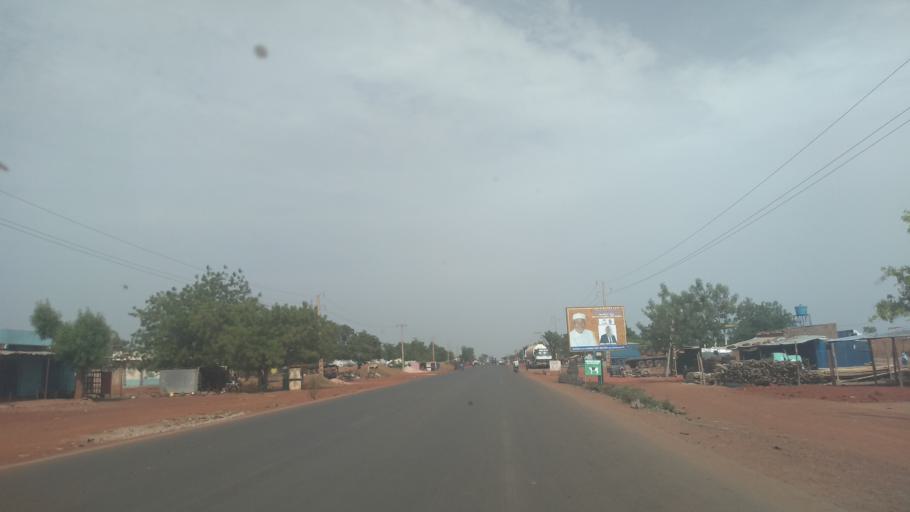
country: ML
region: Bamako
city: Bamako
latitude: 12.5861
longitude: -7.8290
